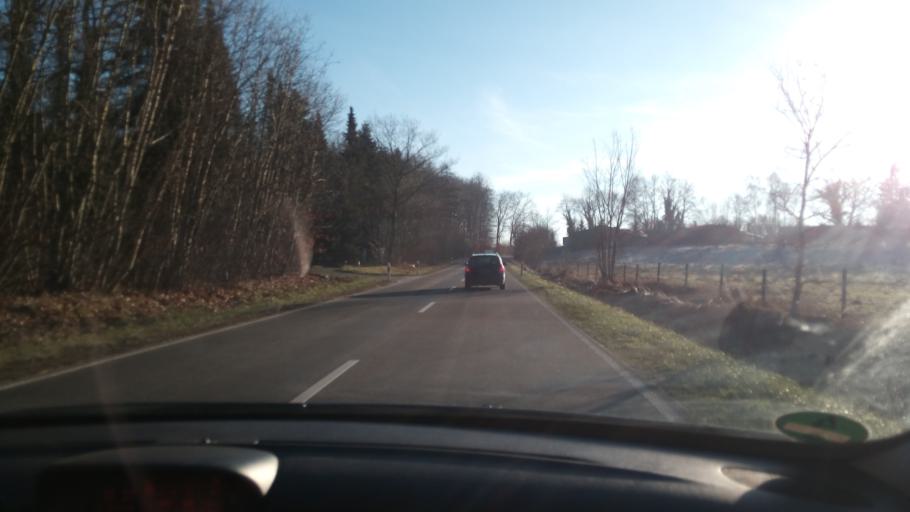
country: DE
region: Schleswig-Holstein
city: Buchhorst
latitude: 53.3917
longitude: 10.5554
